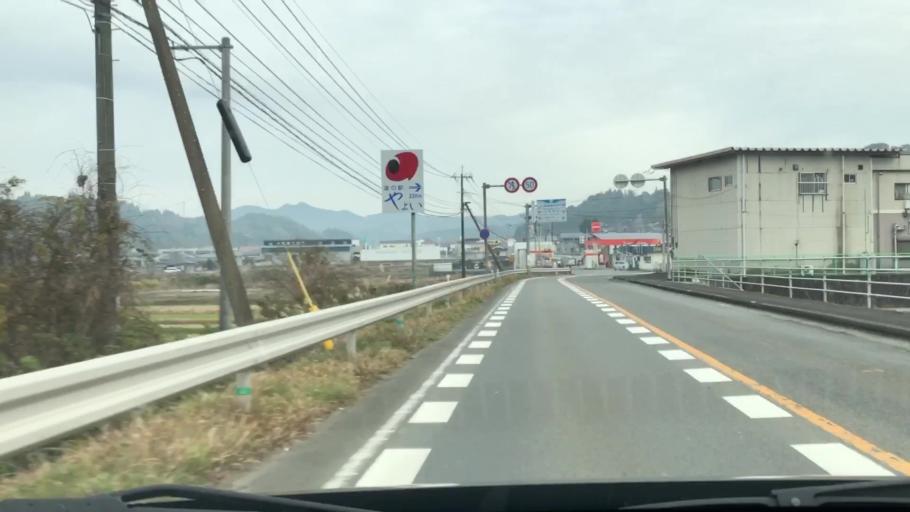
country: JP
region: Oita
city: Usuki
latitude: 33.0318
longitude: 131.6884
